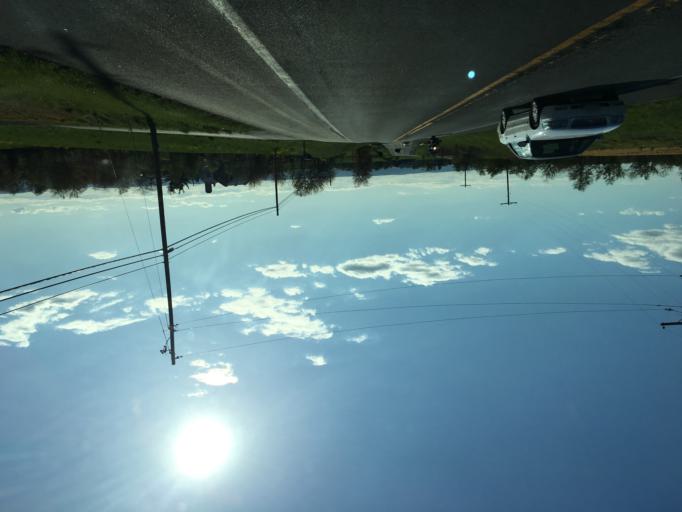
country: US
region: Maryland
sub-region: Frederick County
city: Woodsboro
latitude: 39.5737
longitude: -77.2753
